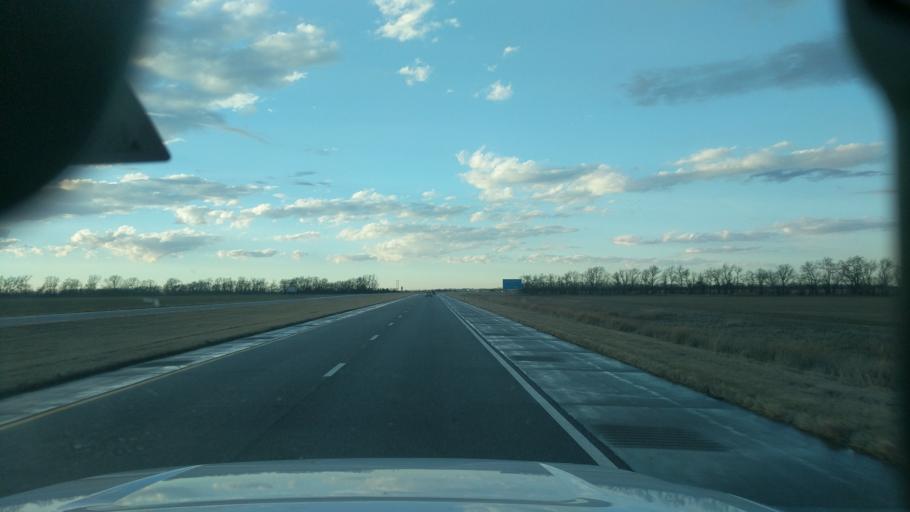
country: US
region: Kansas
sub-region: McPherson County
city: Moundridge
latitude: 38.1931
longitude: -97.4757
